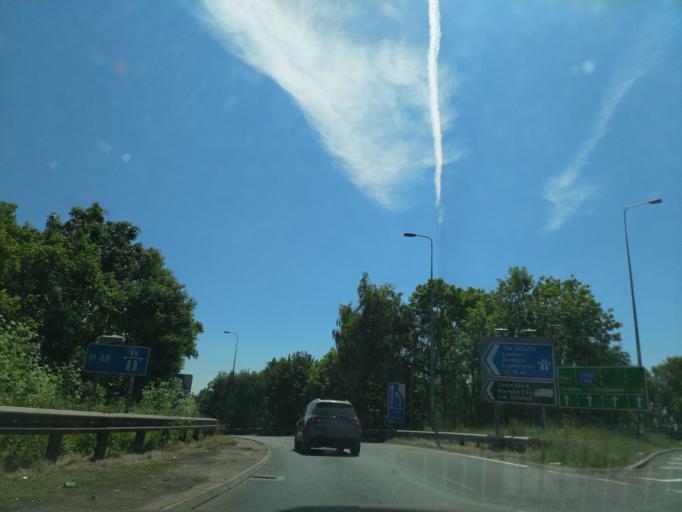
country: GB
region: England
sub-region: Warwickshire
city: Warwick
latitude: 52.2601
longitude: -1.6116
